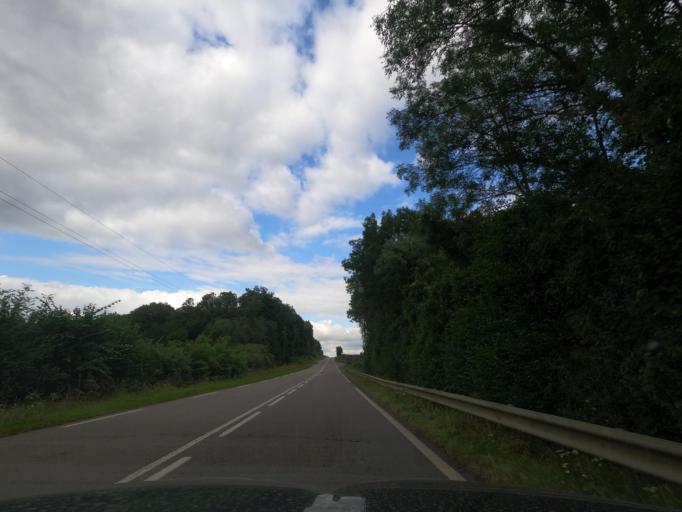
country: FR
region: Lower Normandy
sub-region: Departement de l'Orne
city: Gace
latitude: 48.8832
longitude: 0.3906
